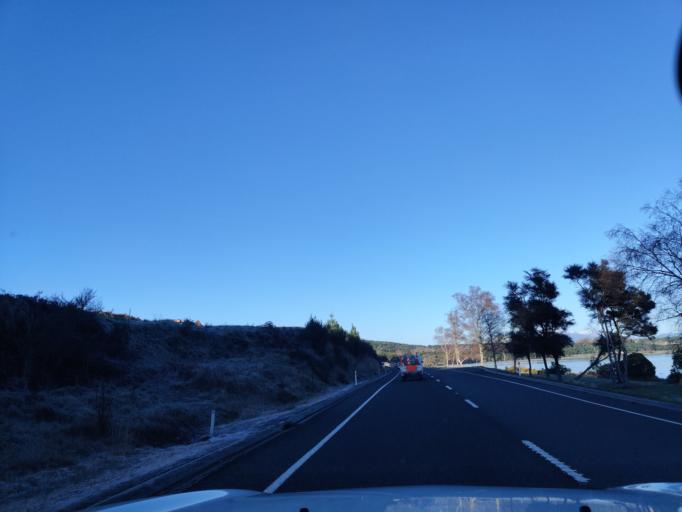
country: NZ
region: Waikato
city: Turangi
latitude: -38.8971
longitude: 175.9463
